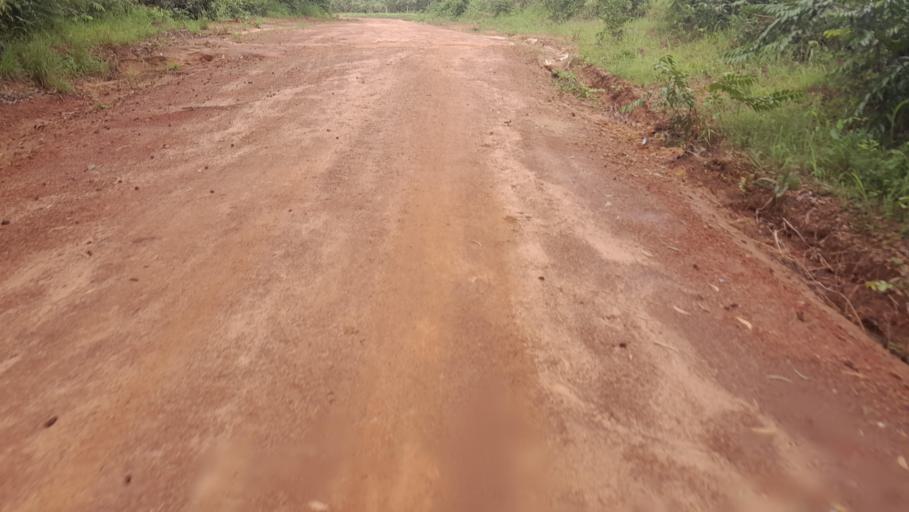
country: GN
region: Boke
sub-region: Boffa
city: Boffa
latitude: 10.0796
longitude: -13.8661
